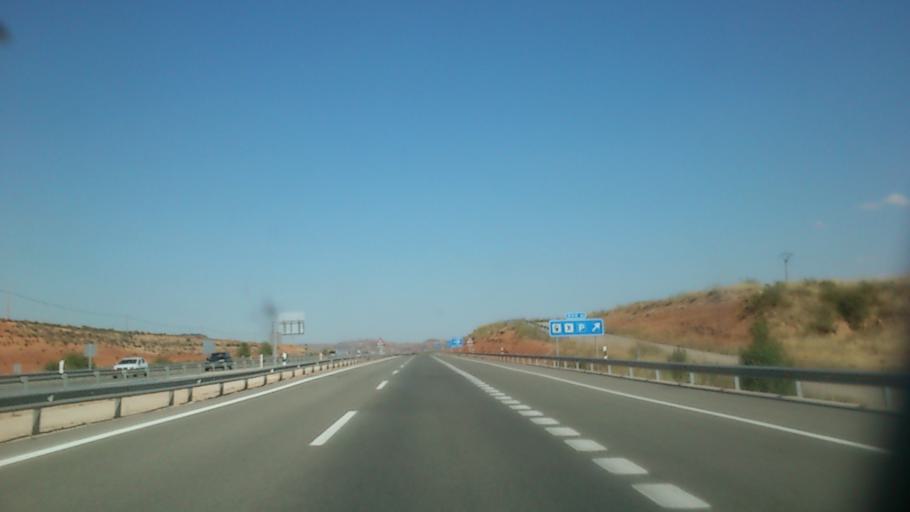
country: ES
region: Aragon
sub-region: Provincia de Zaragoza
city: Cetina
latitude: 41.3036
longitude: -1.9594
